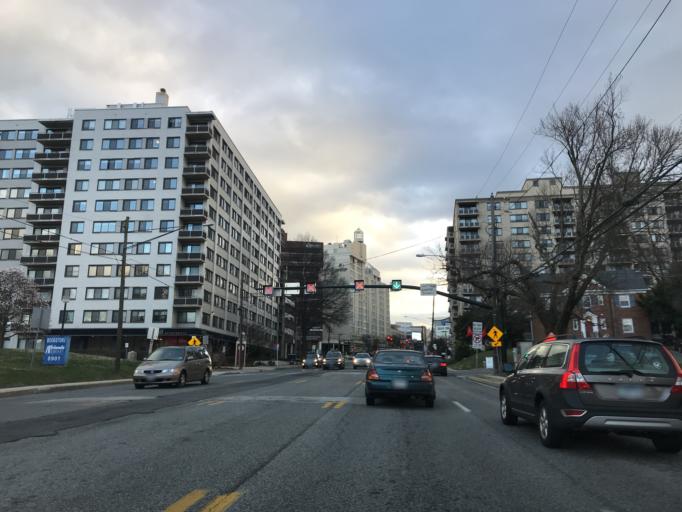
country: US
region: Maryland
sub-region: Montgomery County
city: Silver Spring
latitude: 39.0007
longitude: -77.0256
